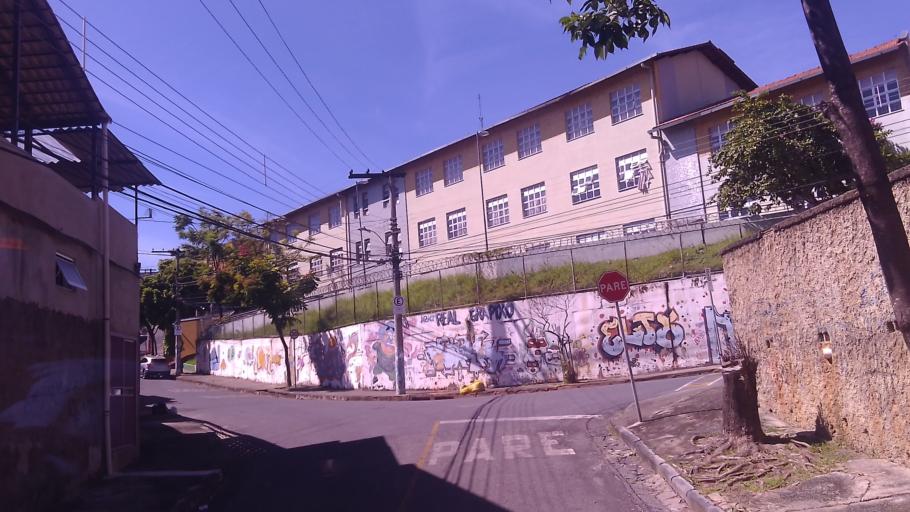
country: BR
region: Minas Gerais
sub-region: Contagem
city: Contagem
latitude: -19.9163
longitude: -44.0002
